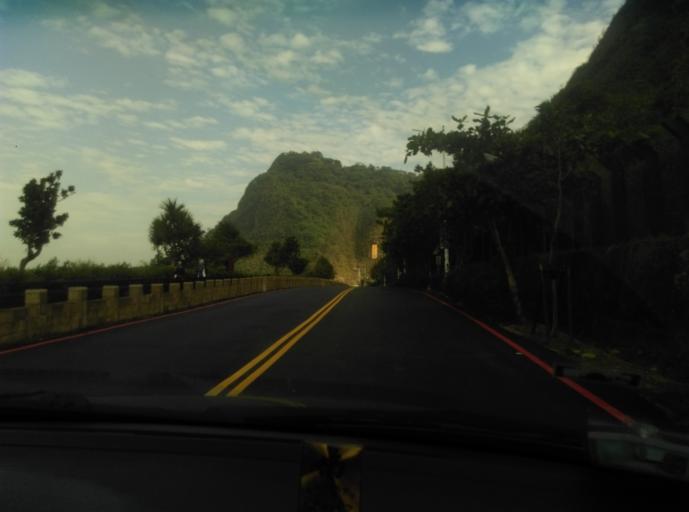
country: TW
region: Taiwan
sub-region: Keelung
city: Keelung
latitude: 25.1639
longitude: 121.7096
